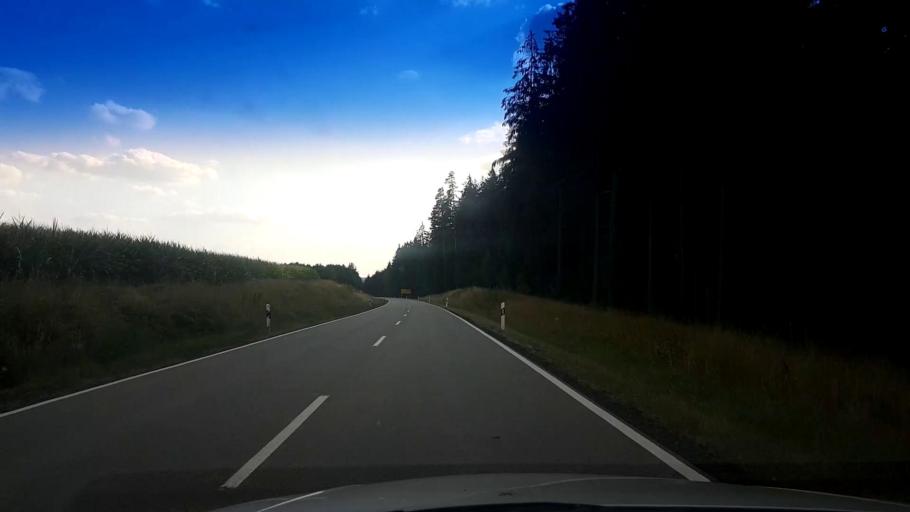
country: DE
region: Bavaria
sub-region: Upper Palatinate
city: Tirschenreuth
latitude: 49.8908
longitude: 12.3699
